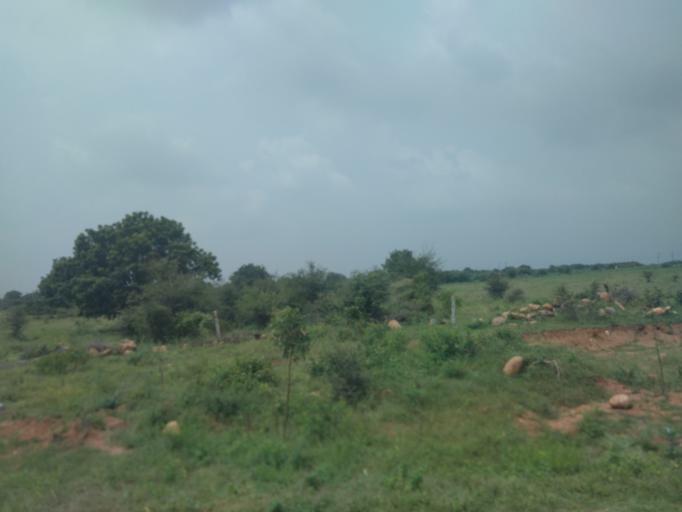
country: IN
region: Telangana
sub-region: Warangal
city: Jangaon
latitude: 17.6677
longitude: 79.0890
